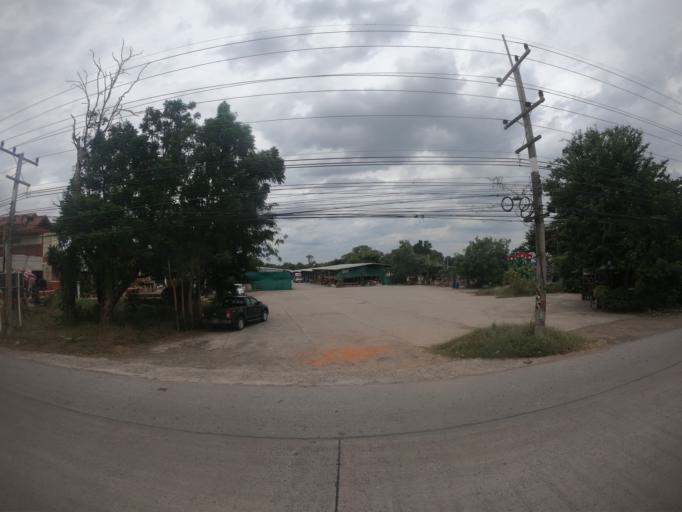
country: TH
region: Nakhon Ratchasima
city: Chok Chai
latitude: 14.7991
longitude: 102.1709
